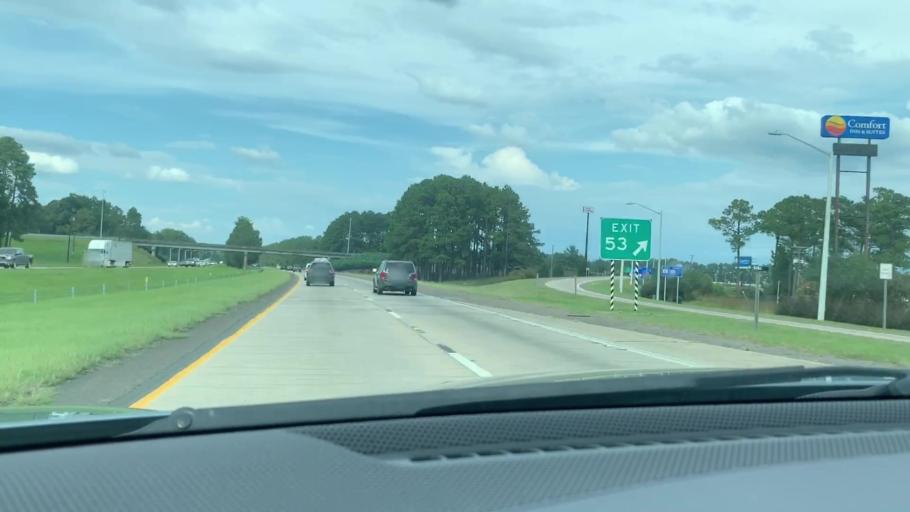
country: US
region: South Carolina
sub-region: Colleton County
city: Walterboro
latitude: 32.8771
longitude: -80.7171
